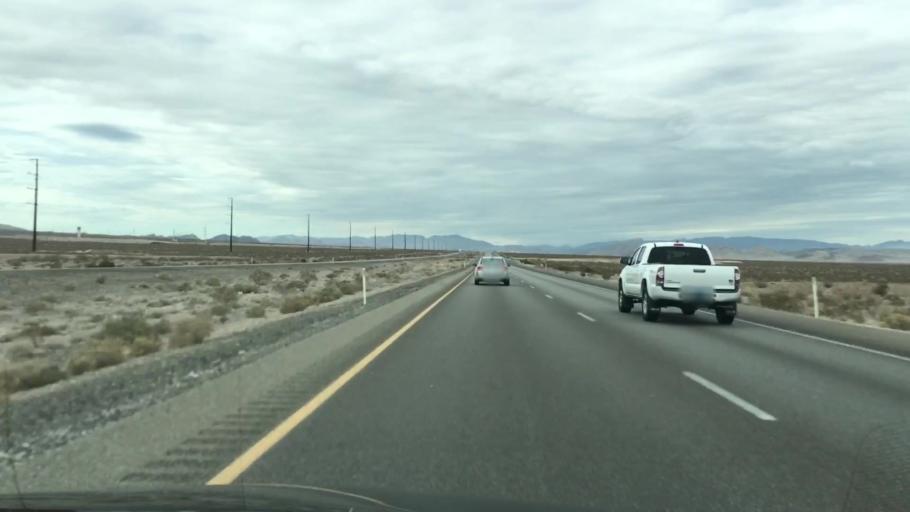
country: US
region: Nevada
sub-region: Clark County
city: Summerlin South
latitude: 36.5160
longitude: -115.5343
